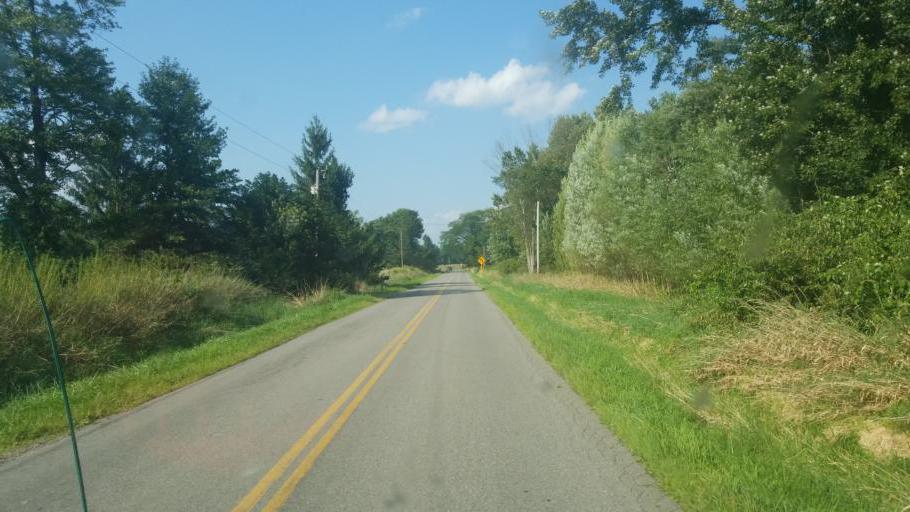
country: US
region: Ohio
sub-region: Medina County
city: Lodi
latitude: 41.0071
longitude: -82.0353
